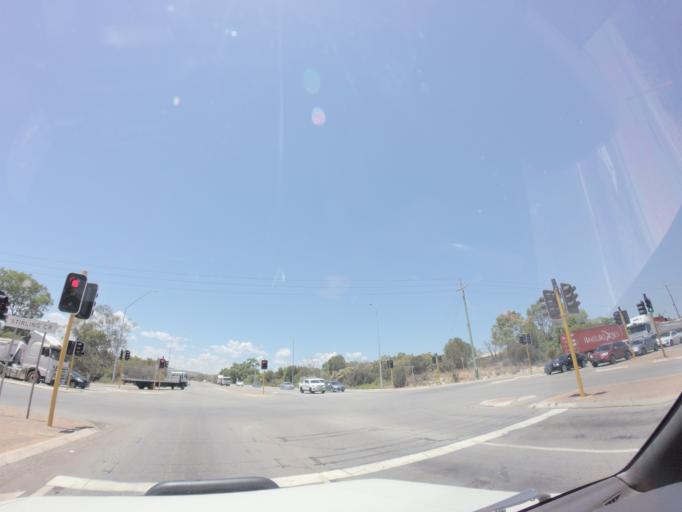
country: AU
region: Western Australia
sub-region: Swan
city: Midland
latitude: -31.9174
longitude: 116.0080
